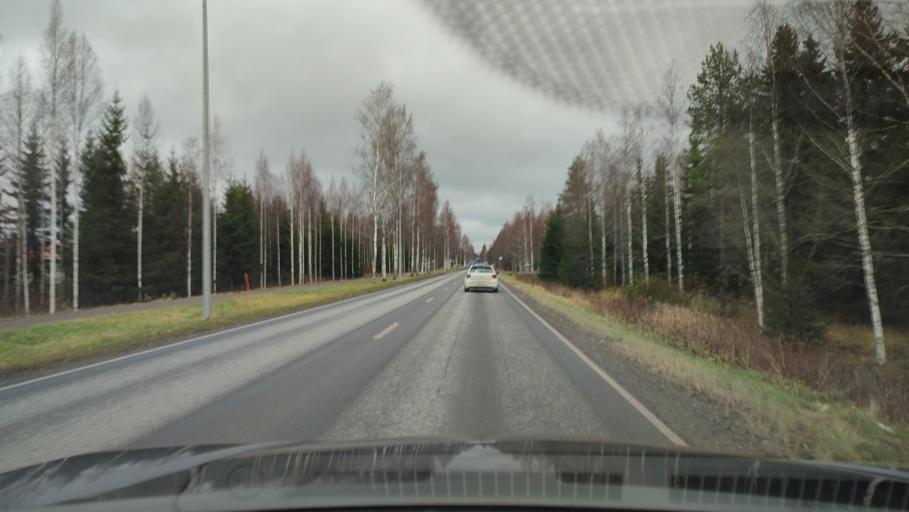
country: FI
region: Southern Ostrobothnia
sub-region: Suupohja
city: Kauhajoki
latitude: 62.4107
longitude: 22.1682
